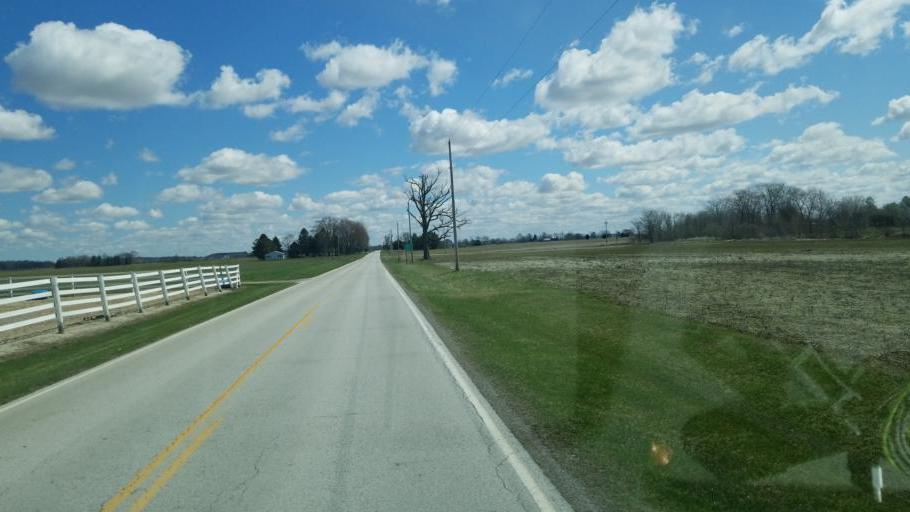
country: US
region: Ohio
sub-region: Hancock County
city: Findlay
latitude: 41.0371
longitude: -83.5137
